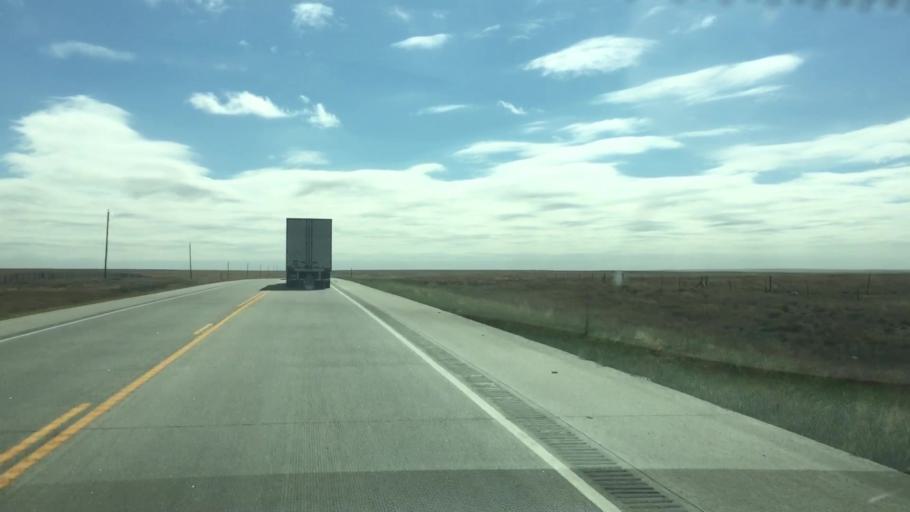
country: US
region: Colorado
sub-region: Lincoln County
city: Hugo
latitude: 39.0239
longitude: -103.3157
